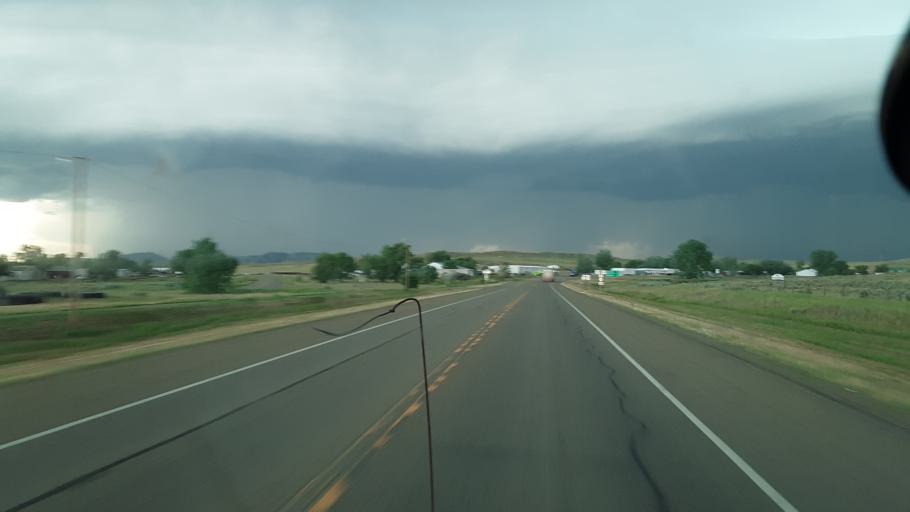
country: US
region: Montana
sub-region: Powder River County
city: Broadus
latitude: 45.4435
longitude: -105.4168
